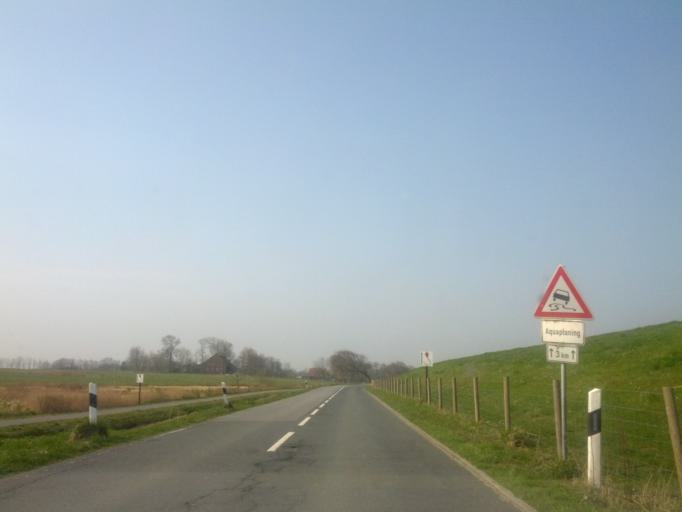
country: DE
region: Lower Saxony
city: Holtgast
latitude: 53.6728
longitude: 7.5584
